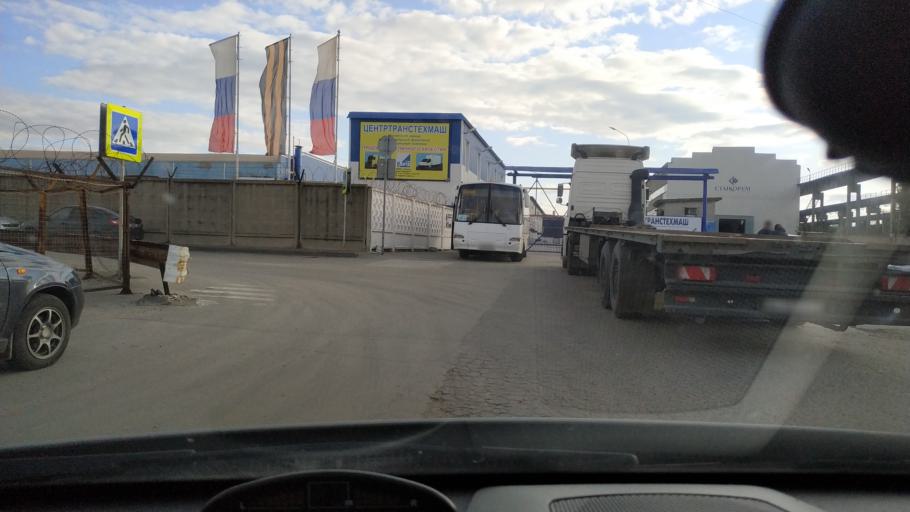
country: RU
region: Rjazan
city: Polyany
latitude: 54.5791
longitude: 39.8381
